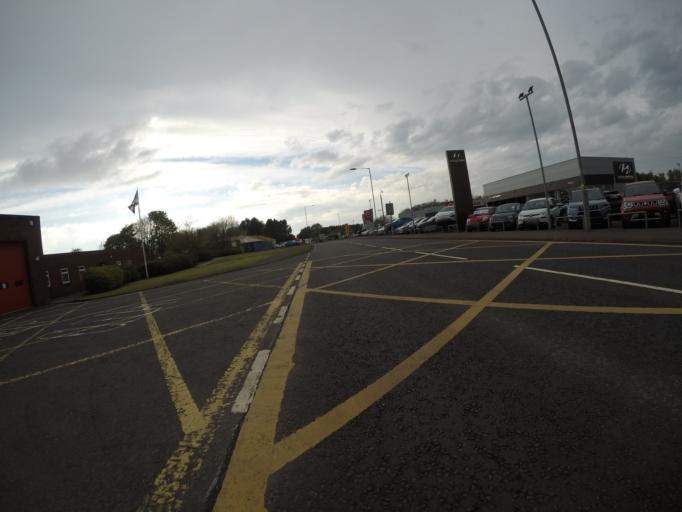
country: GB
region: Scotland
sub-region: North Ayrshire
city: Dreghorn
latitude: 55.6077
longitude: -4.6347
